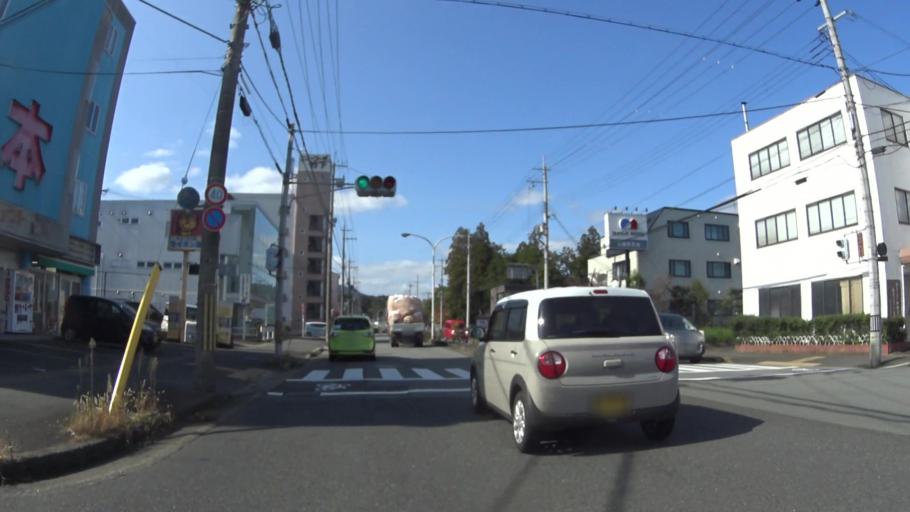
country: JP
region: Kyoto
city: Fukuchiyama
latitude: 35.3017
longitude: 135.1157
